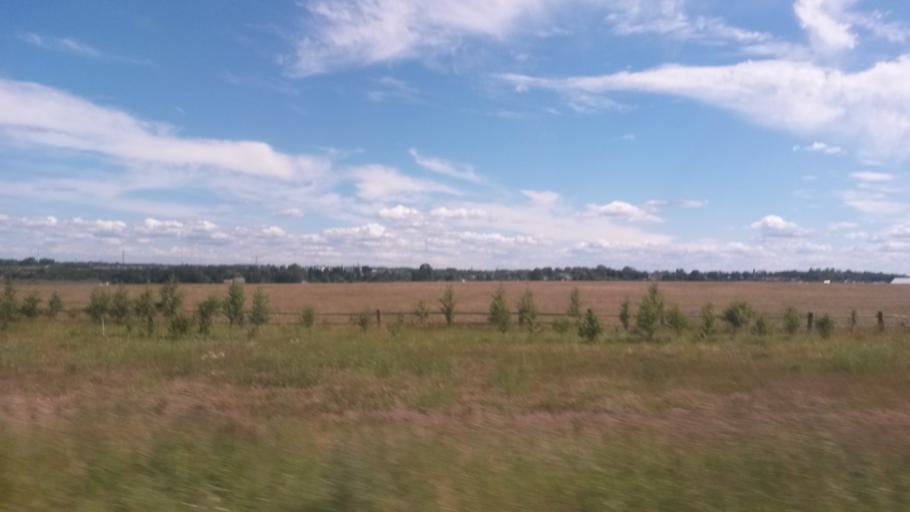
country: RU
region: Ivanovo
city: Staraya Vichuga
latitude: 57.2298
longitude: 41.8667
